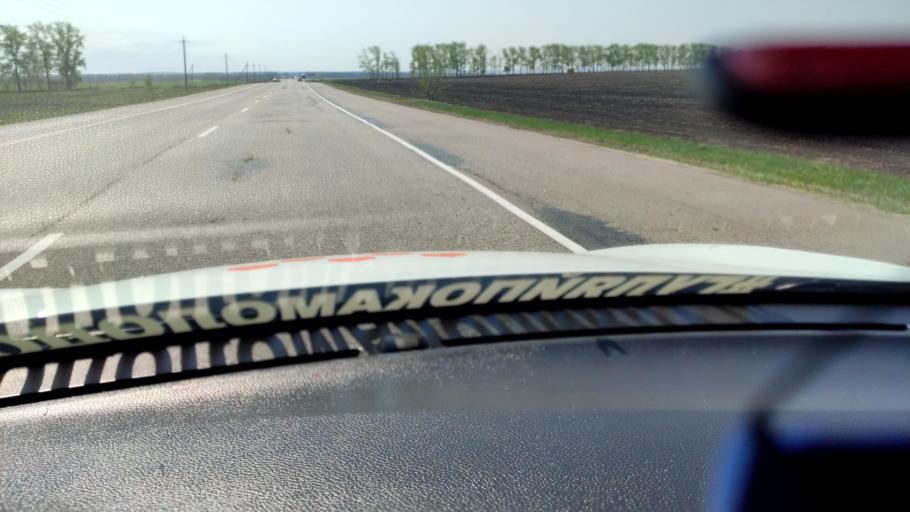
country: RU
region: Voronezj
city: Strelitsa
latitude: 51.5357
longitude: 38.9699
